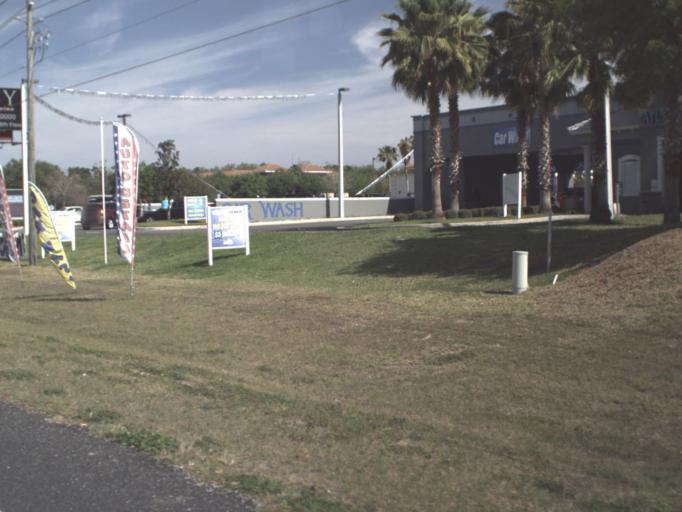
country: US
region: Florida
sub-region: Sumter County
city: The Villages
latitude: 28.9565
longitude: -81.9614
